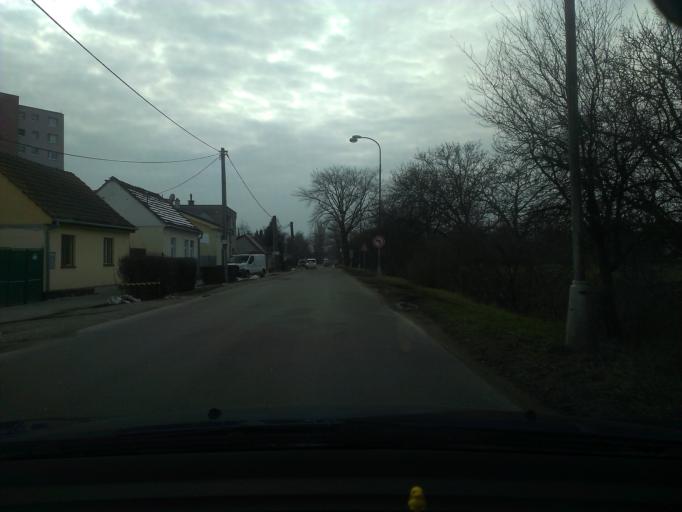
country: SK
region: Trnavsky
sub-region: Okres Trnava
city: Piestany
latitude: 48.5927
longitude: 17.8043
